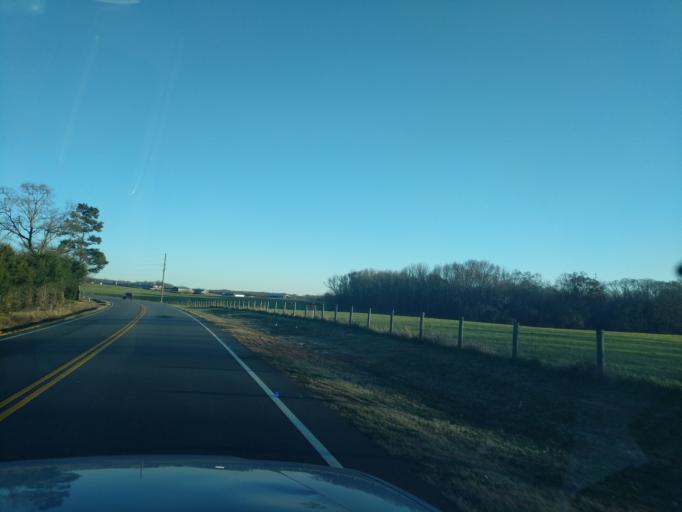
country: US
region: South Carolina
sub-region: Oconee County
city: Utica
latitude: 34.5859
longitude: -82.9479
